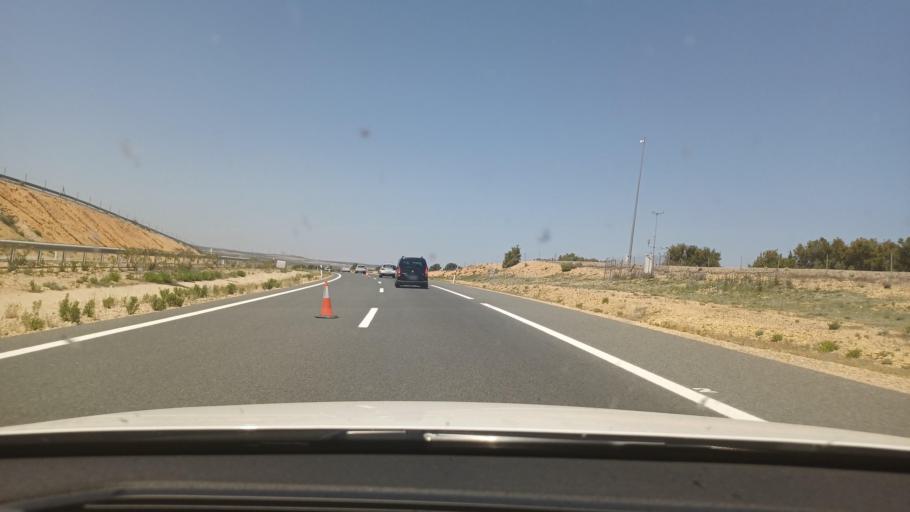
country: ES
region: Castille-La Mancha
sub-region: Provincia de Albacete
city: Alpera
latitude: 38.8796
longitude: -1.2000
